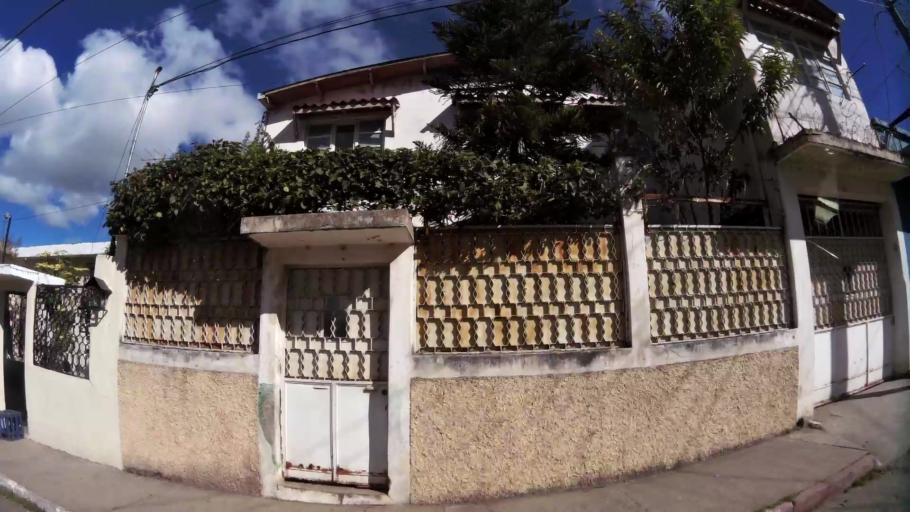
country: GT
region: Quetzaltenango
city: Quetzaltenango
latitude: 14.8358
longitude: -91.5052
